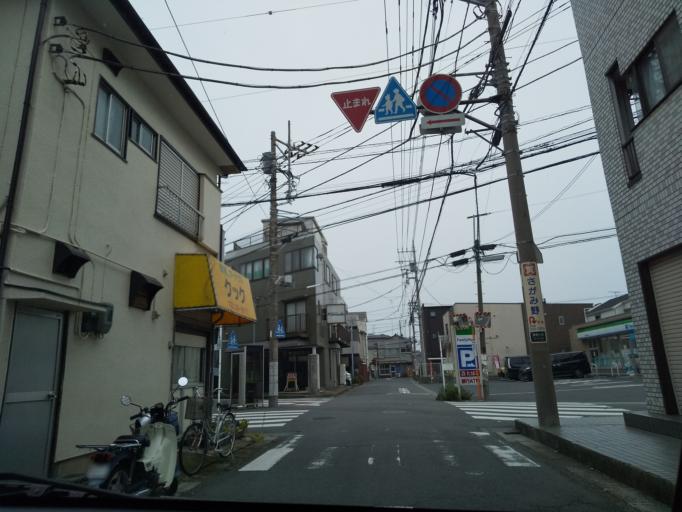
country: JP
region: Kanagawa
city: Minami-rinkan
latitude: 35.4675
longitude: 139.4252
